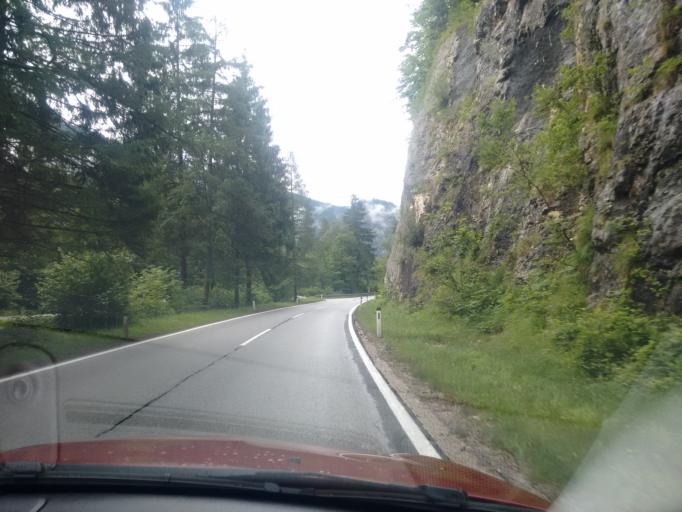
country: AT
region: Upper Austria
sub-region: Politischer Bezirk Gmunden
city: Bad Goisern
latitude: 47.5879
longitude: 13.6568
